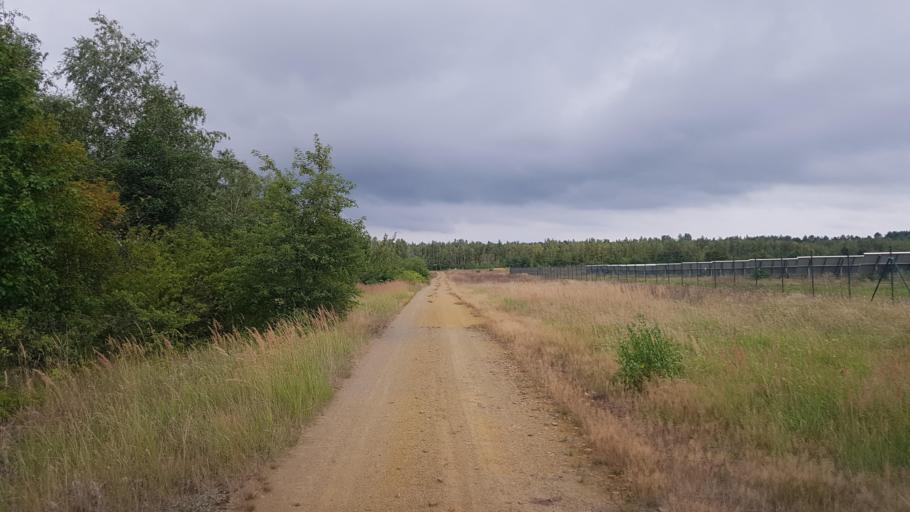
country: DE
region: Brandenburg
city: Finsterwalde
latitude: 51.5646
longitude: 13.7284
